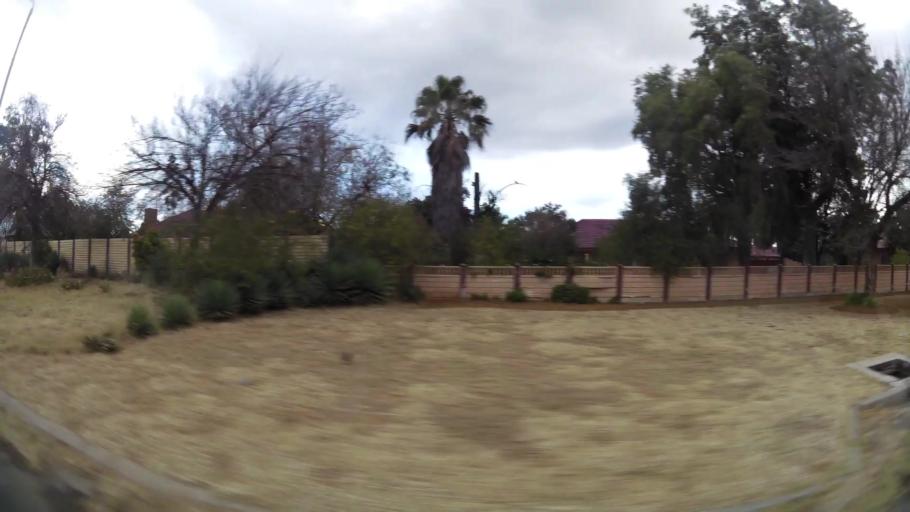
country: ZA
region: Orange Free State
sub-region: Lejweleputswa District Municipality
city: Welkom
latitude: -27.9618
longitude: 26.7215
